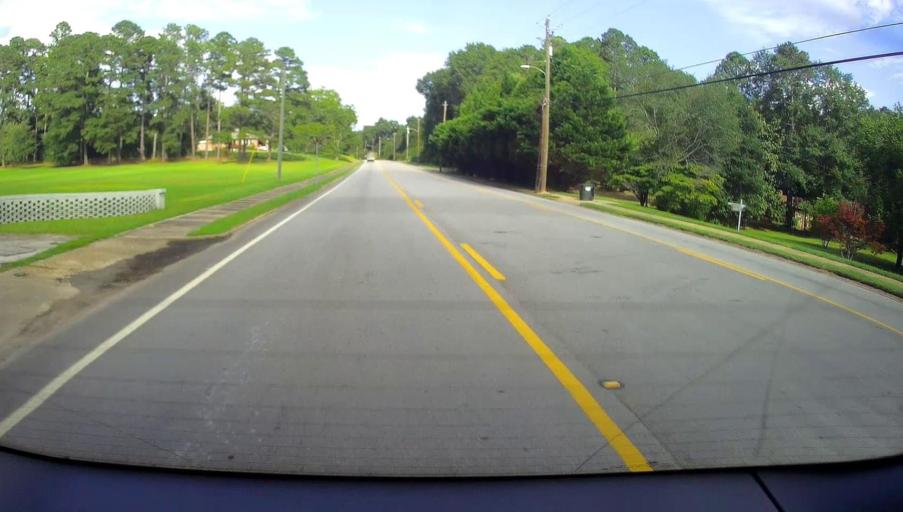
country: US
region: Georgia
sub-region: Meriwether County
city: Manchester
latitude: 32.9830
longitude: -84.5928
